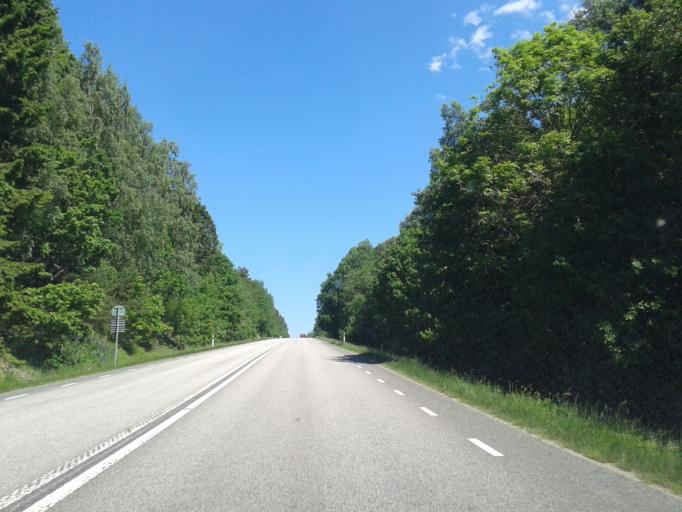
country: SE
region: Vaestra Goetaland
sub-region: Orust
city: Henan
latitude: 58.2844
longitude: 11.6982
